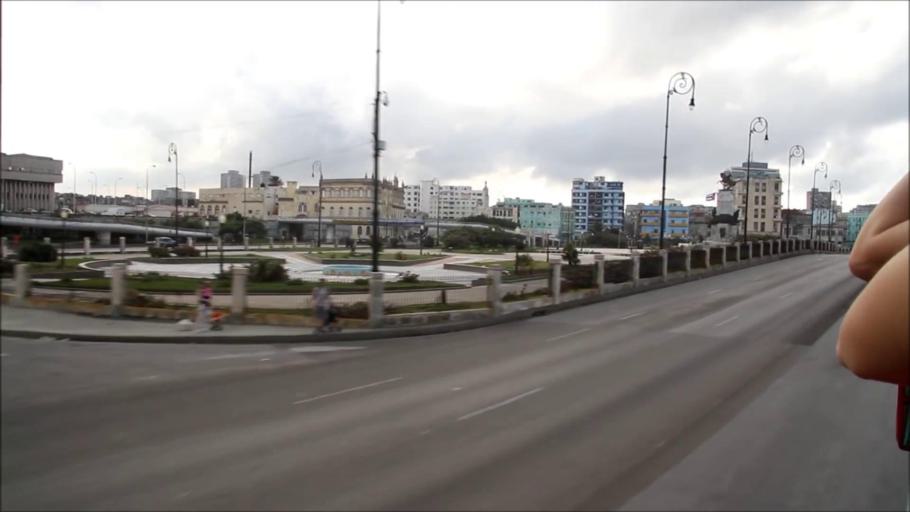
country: CU
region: La Habana
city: Centro Habana
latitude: 23.1416
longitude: -82.3708
